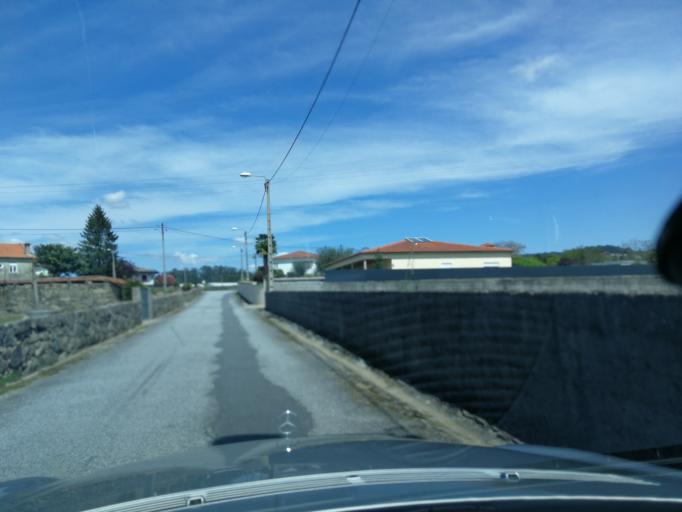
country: PT
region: Braga
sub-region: Vila Nova de Famalicao
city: Vila Nova de Famalicao
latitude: 41.4320
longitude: -8.5277
